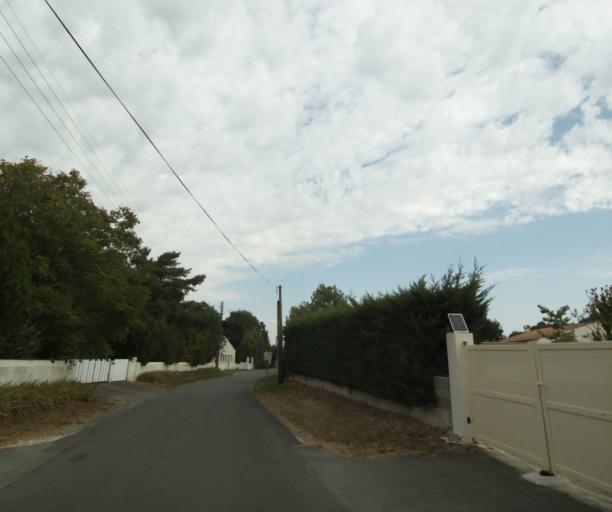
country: FR
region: Poitou-Charentes
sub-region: Departement de la Charente-Maritime
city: Tonnay-Charente
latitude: 45.9634
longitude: -0.8724
